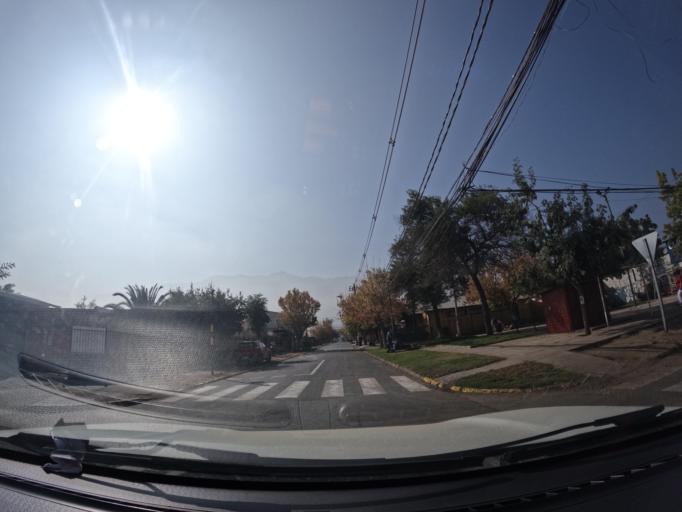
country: CL
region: Santiago Metropolitan
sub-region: Provincia de Santiago
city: Villa Presidente Frei, Nunoa, Santiago, Chile
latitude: -33.4729
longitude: -70.5465
